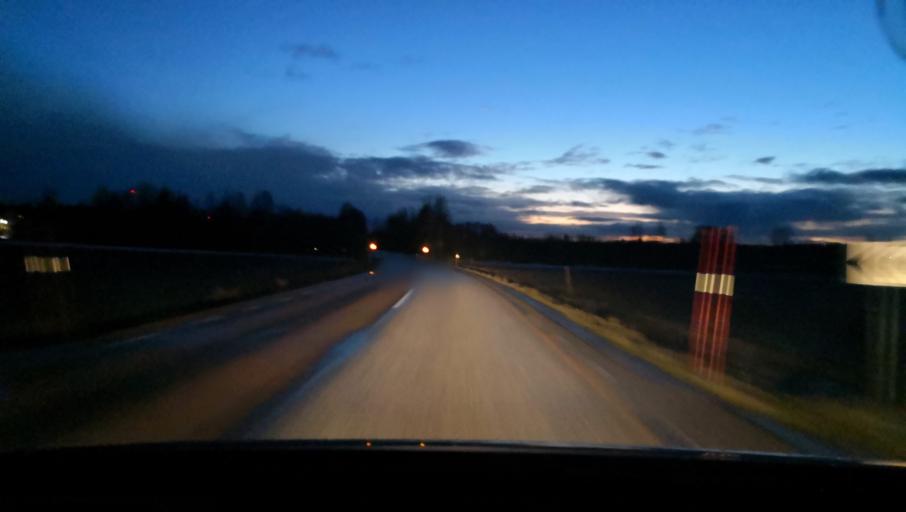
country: SE
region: Vaestmanland
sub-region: Vasteras
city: Skultuna
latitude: 59.7339
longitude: 16.4352
